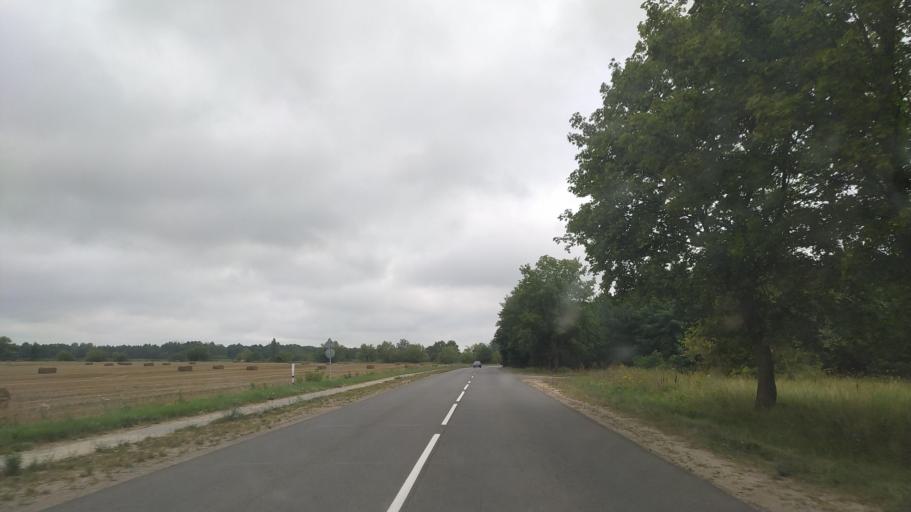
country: BY
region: Brest
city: Byaroza
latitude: 52.5559
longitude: 24.9195
